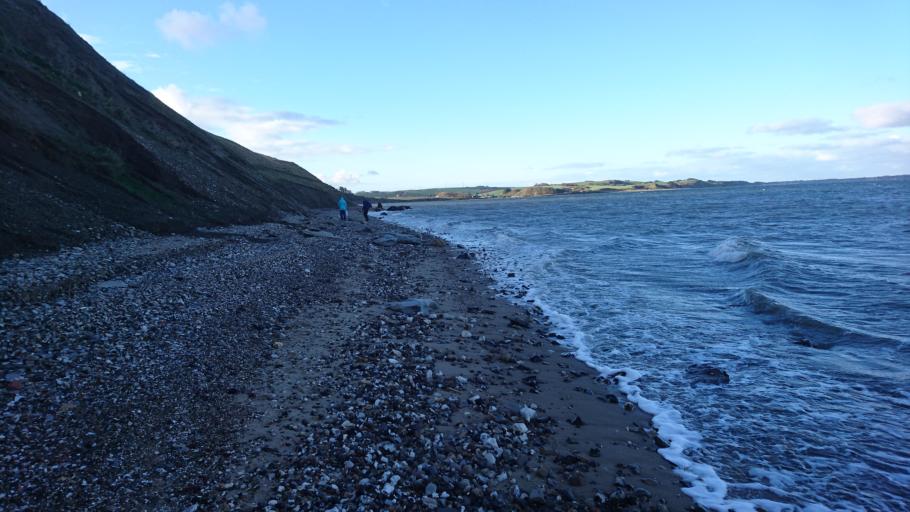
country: DK
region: North Denmark
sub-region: Thisted Kommune
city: Thisted
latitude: 56.8960
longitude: 8.7515
